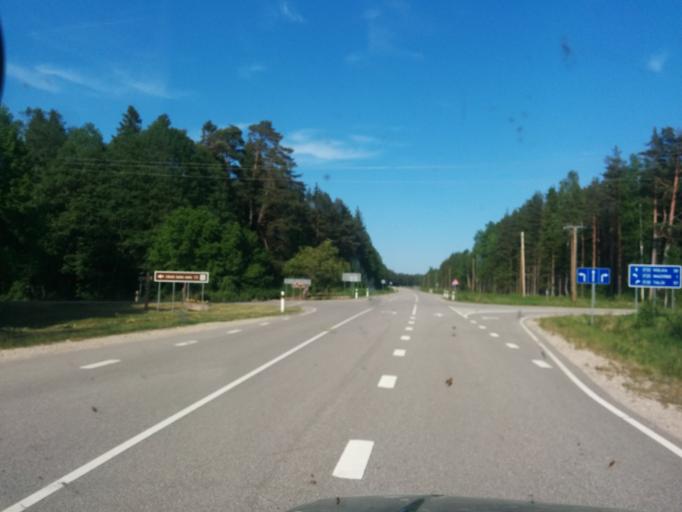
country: LV
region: Dundaga
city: Dundaga
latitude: 57.6738
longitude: 22.3227
